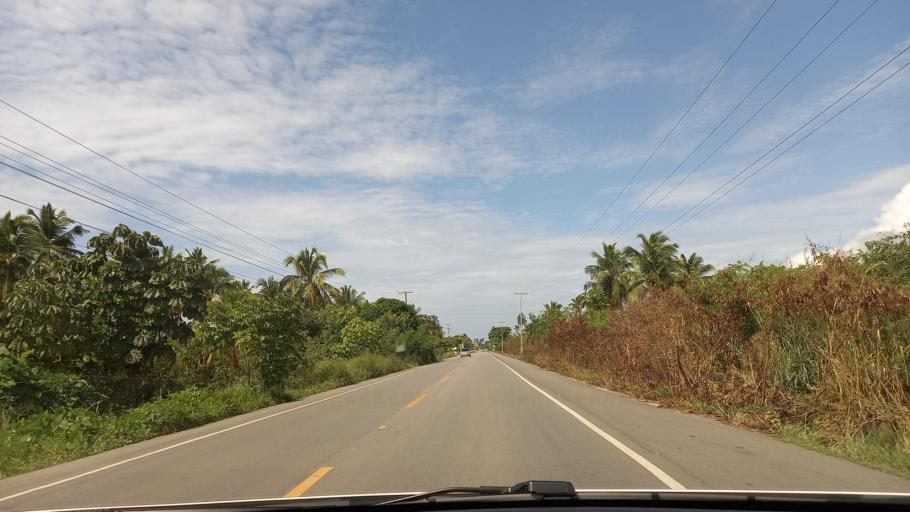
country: BR
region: Alagoas
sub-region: Maragogi
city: Maragogi
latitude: -8.9664
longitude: -35.1817
